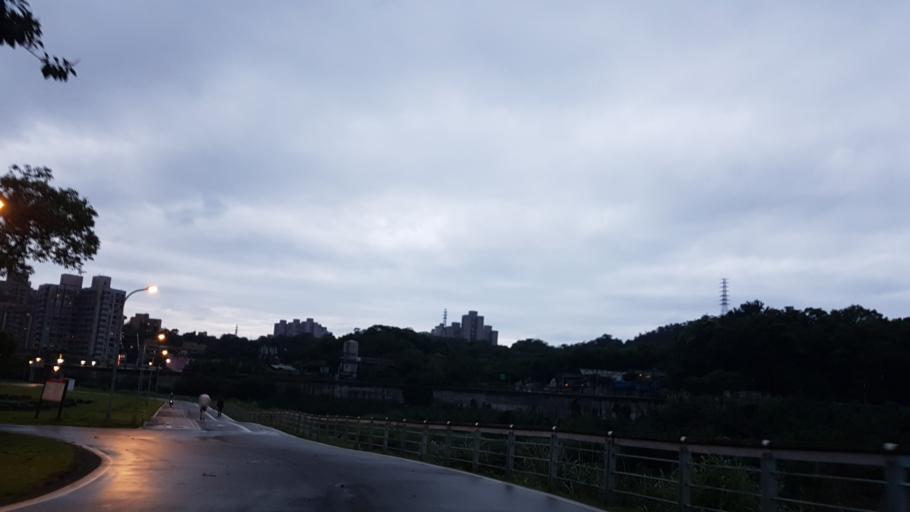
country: TW
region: Taipei
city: Taipei
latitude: 24.9992
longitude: 121.5795
